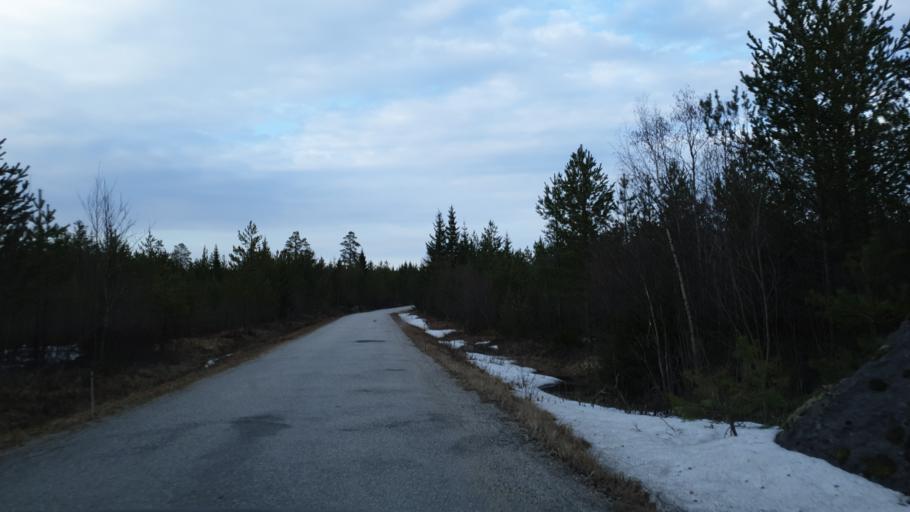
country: SE
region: Vaesternorrland
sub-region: Sundsvalls Kommun
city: Njurundabommen
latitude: 62.0284
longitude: 17.4045
